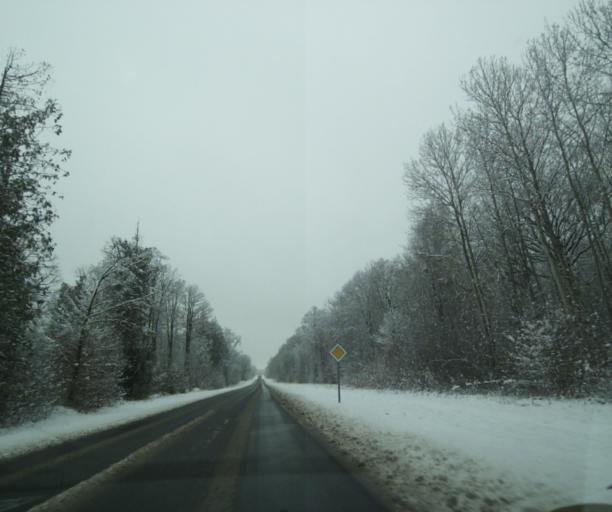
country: FR
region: Champagne-Ardenne
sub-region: Departement de la Haute-Marne
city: Laneuville-a-Remy
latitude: 48.5569
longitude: 4.8394
